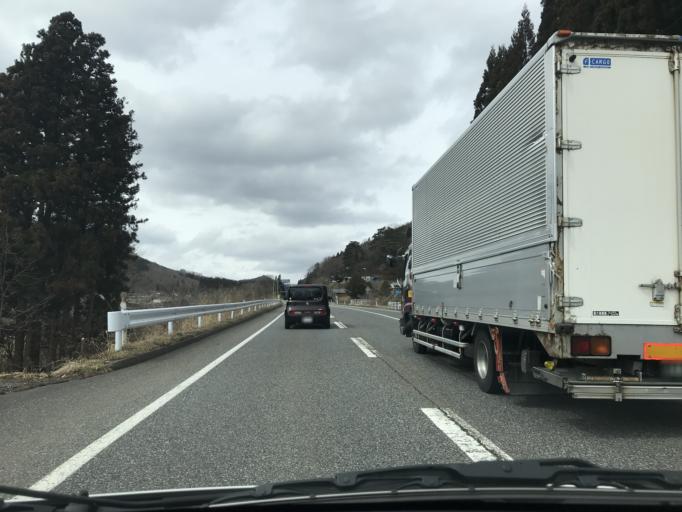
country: JP
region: Iwate
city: Tono
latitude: 39.3385
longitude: 141.4431
